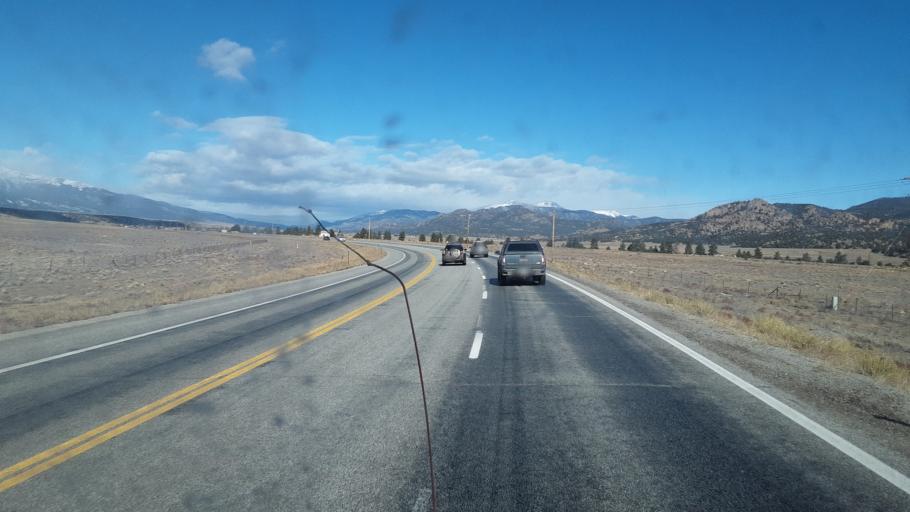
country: US
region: Colorado
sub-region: Chaffee County
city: Buena Vista
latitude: 38.7521
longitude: -106.0813
